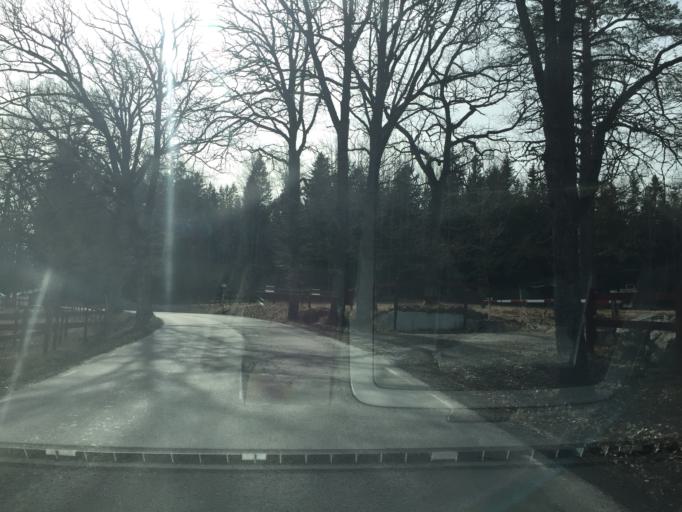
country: SE
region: Stockholm
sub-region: Botkyrka Kommun
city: Tullinge
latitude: 59.1075
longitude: 17.9751
